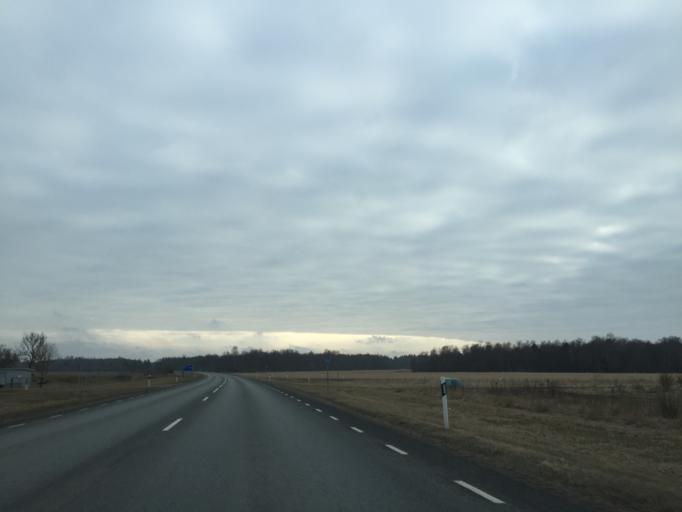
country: EE
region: Saare
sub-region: Orissaare vald
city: Orissaare
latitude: 58.5135
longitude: 22.8778
